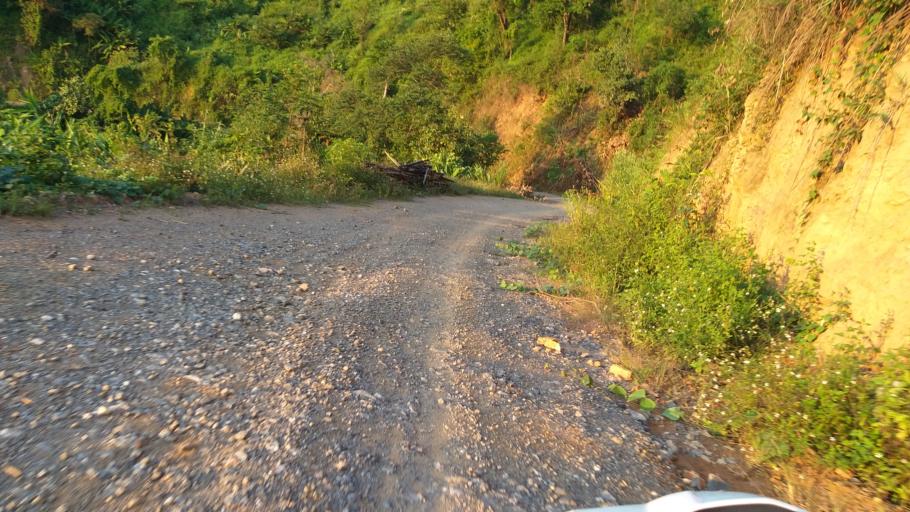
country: LA
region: Phongsali
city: Khoa
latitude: 21.1880
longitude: 102.5433
